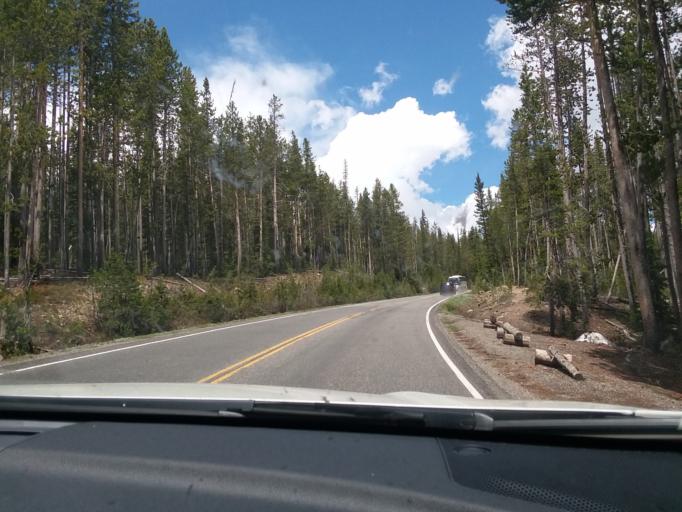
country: US
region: Montana
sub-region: Gallatin County
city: West Yellowstone
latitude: 44.1928
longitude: -110.6580
